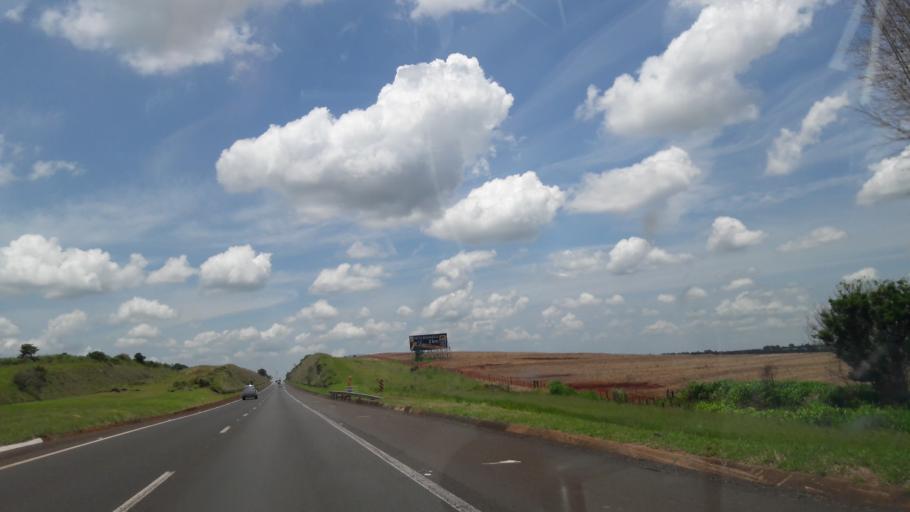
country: BR
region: Sao Paulo
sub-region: Avare
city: Avare
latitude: -22.9547
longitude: -48.8315
